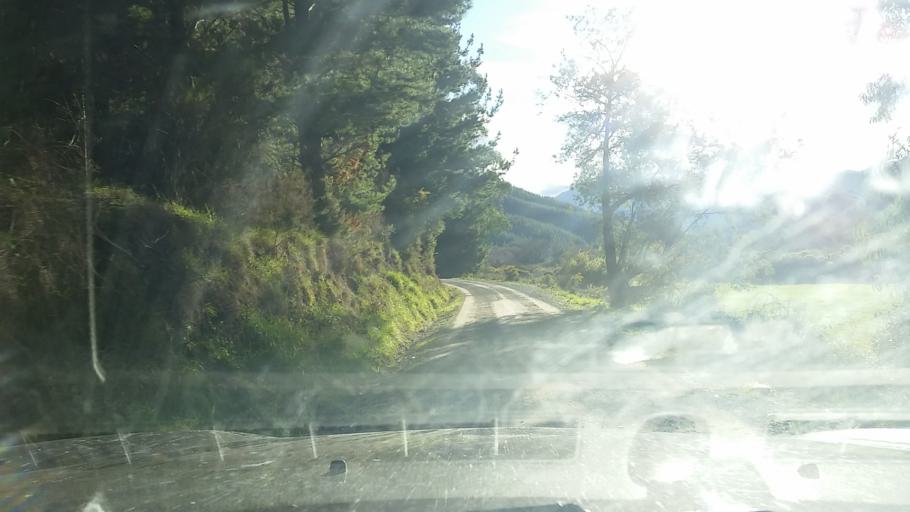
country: NZ
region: Nelson
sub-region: Nelson City
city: Nelson
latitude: -41.5648
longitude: 173.4417
